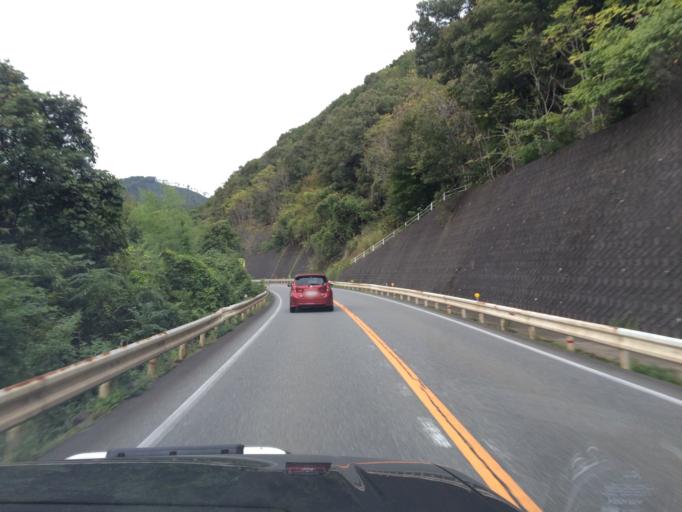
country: JP
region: Hyogo
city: Toyooka
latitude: 35.3684
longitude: 134.8214
